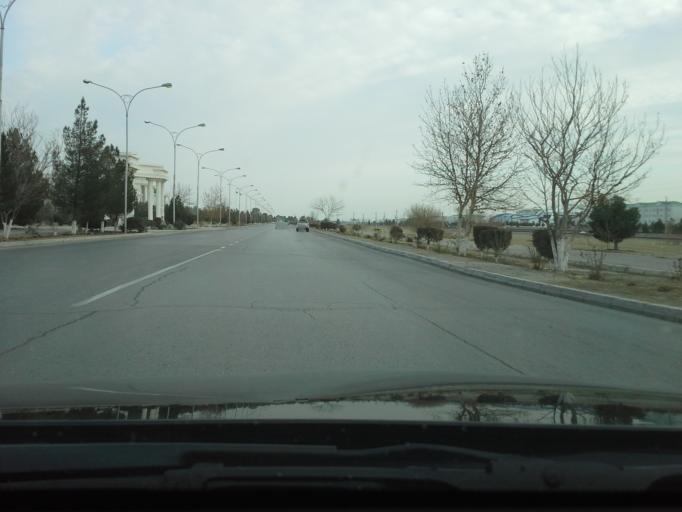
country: TM
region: Ahal
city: Ashgabat
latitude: 37.9915
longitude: 58.3214
